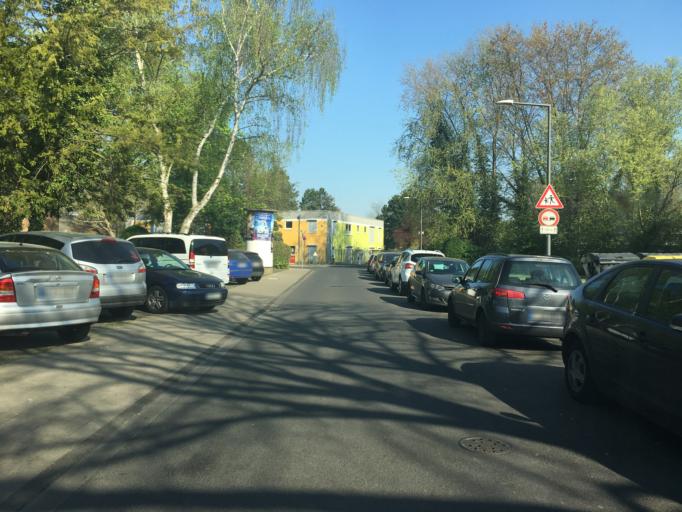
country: DE
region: North Rhine-Westphalia
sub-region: Regierungsbezirk Koln
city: Muelheim
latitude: 50.9960
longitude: 6.9907
